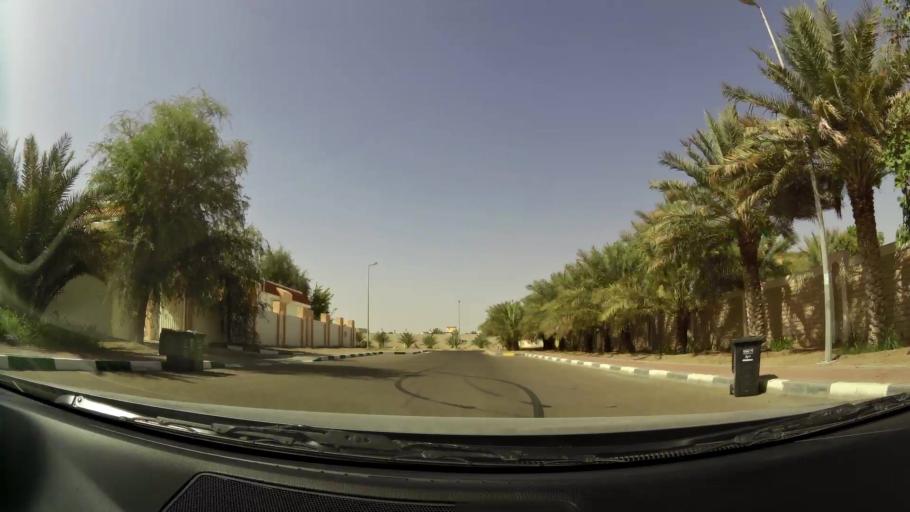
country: OM
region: Al Buraimi
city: Al Buraymi
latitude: 24.3026
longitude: 55.8004
